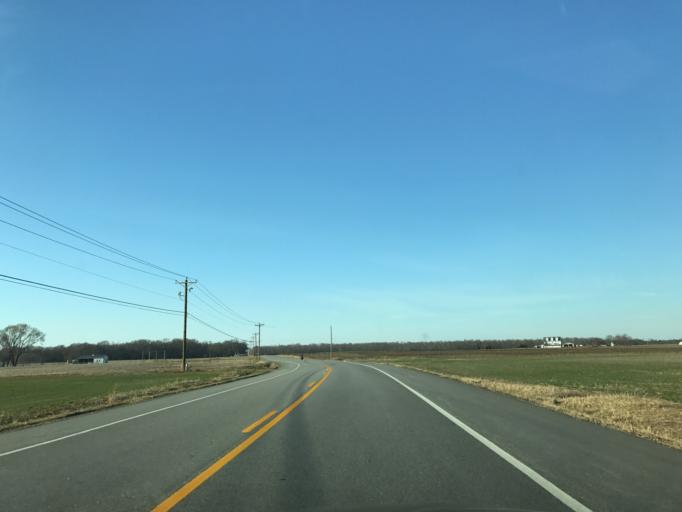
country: US
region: Maryland
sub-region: Queen Anne's County
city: Kingstown
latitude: 39.2192
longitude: -75.8655
